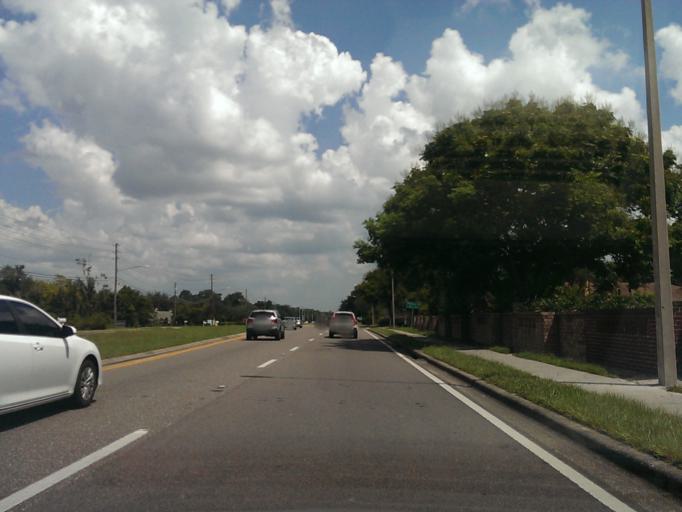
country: US
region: Florida
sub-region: Orange County
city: Bay Hill
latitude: 28.4936
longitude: -81.4873
